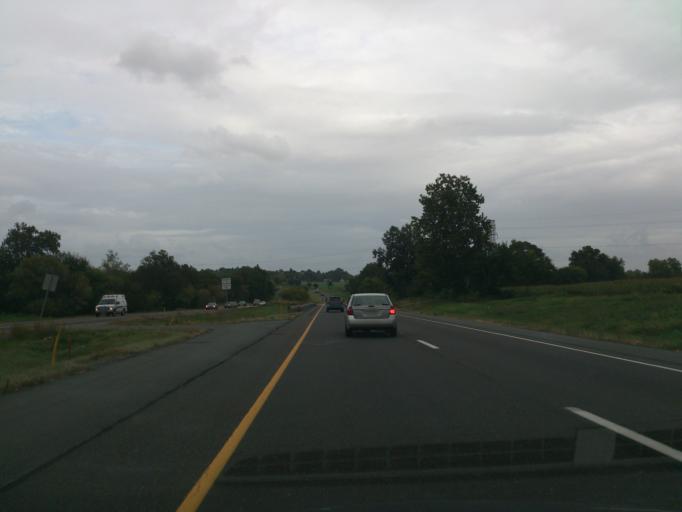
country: US
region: Pennsylvania
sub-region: Lancaster County
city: Brownstown
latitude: 40.1163
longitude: -76.2348
